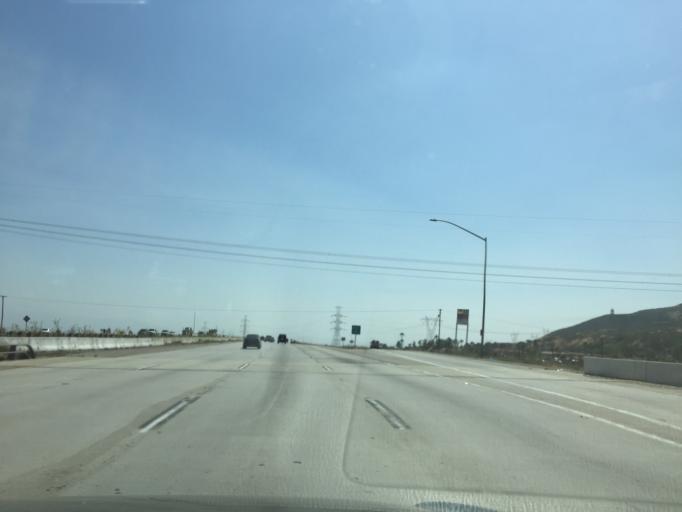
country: US
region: California
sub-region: San Bernardino County
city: Fontana
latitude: 34.1844
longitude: -117.4341
